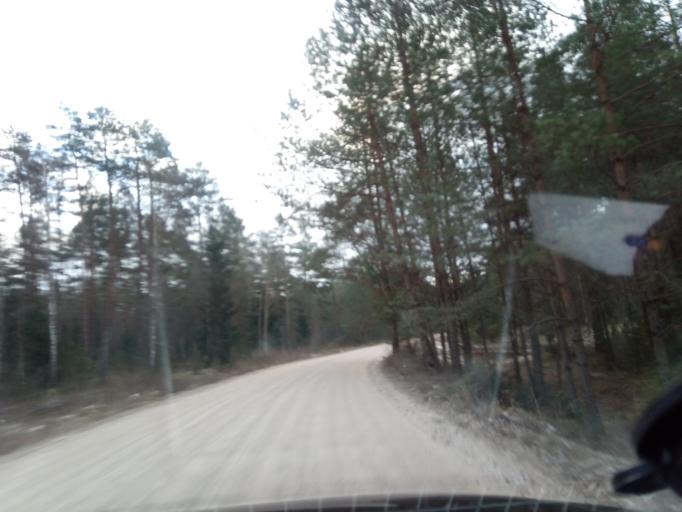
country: LT
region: Alytaus apskritis
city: Varena
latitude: 54.0183
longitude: 24.3512
